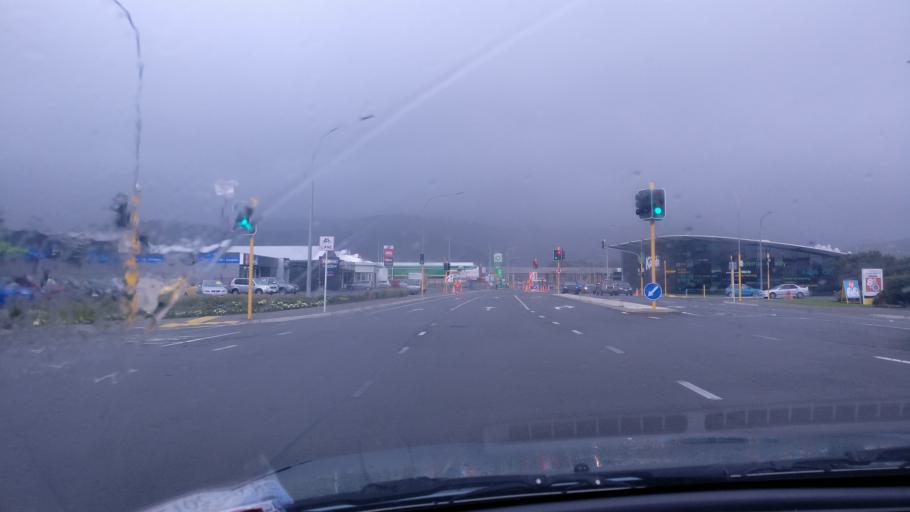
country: NZ
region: Wellington
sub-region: Kapiti Coast District
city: Paraparaumu
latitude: -40.9062
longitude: 174.9977
